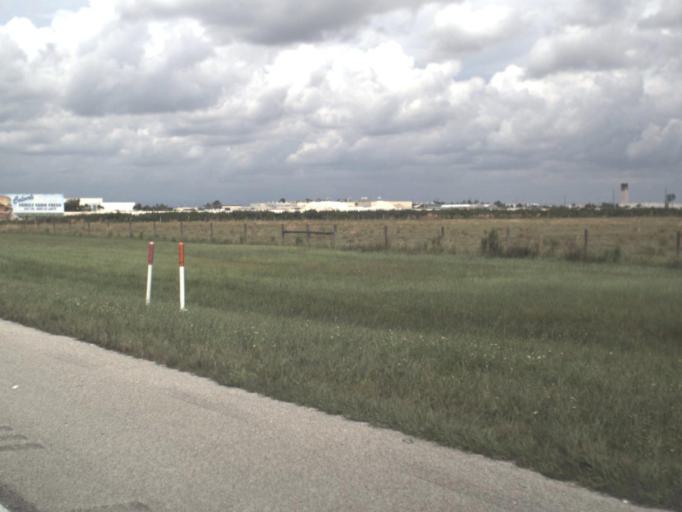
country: US
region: Florida
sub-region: Charlotte County
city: Punta Gorda
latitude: 26.9082
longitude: -82.0095
